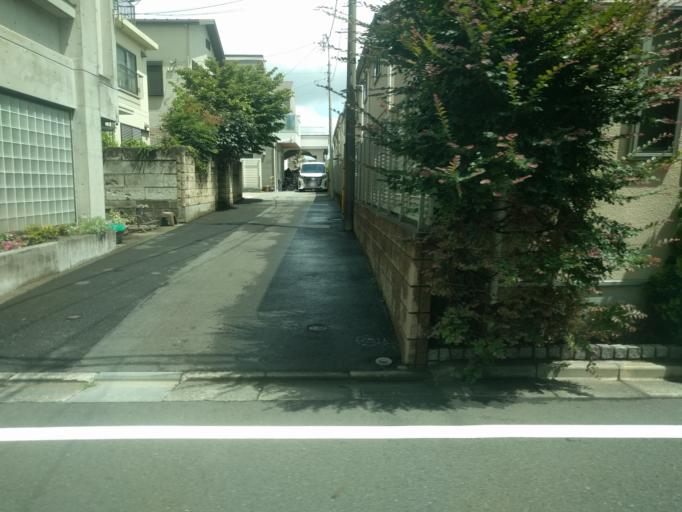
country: JP
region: Kanagawa
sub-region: Kawasaki-shi
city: Kawasaki
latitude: 35.5953
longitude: 139.6769
